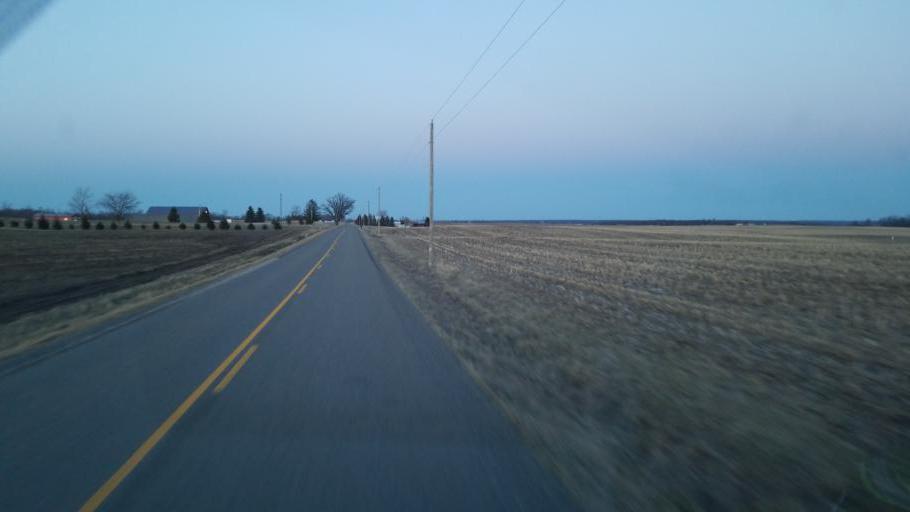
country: US
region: Ohio
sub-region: Champaign County
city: North Lewisburg
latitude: 40.2400
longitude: -83.6107
